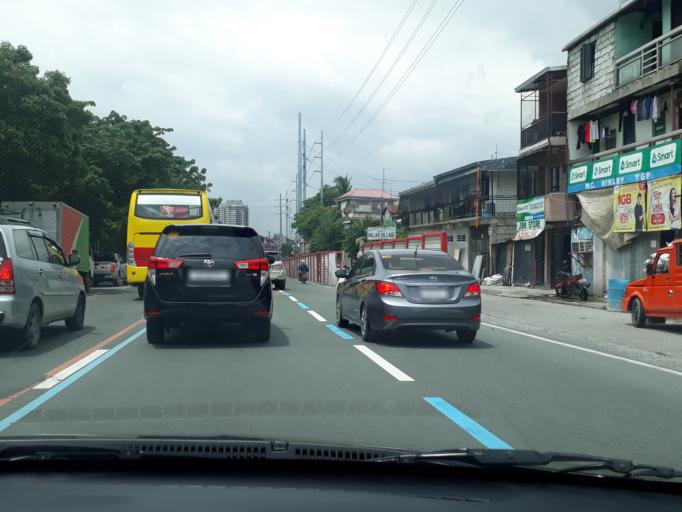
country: PH
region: Calabarzon
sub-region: Province of Rizal
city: Pateros
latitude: 14.5378
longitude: 121.0573
